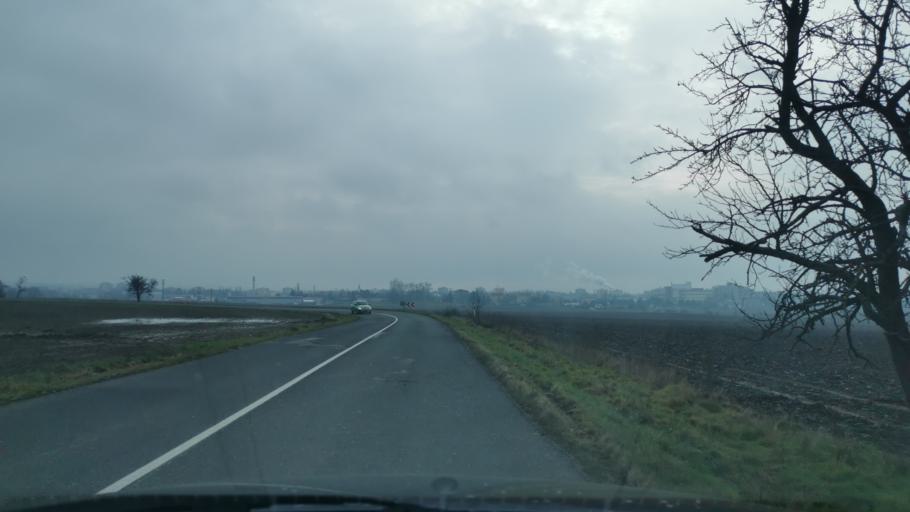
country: SK
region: Trnavsky
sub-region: Okres Senica
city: Senica
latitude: 48.6924
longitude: 17.3559
